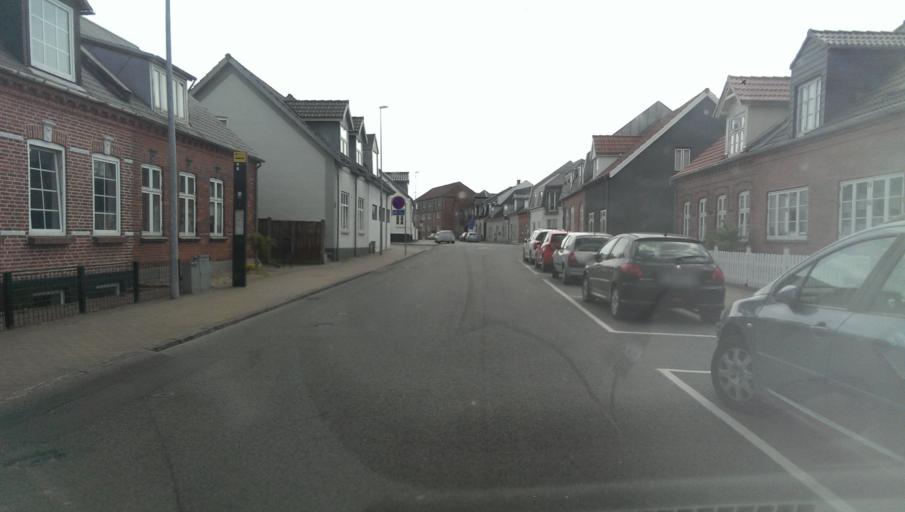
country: DK
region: South Denmark
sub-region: Esbjerg Kommune
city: Esbjerg
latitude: 55.4761
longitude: 8.4610
